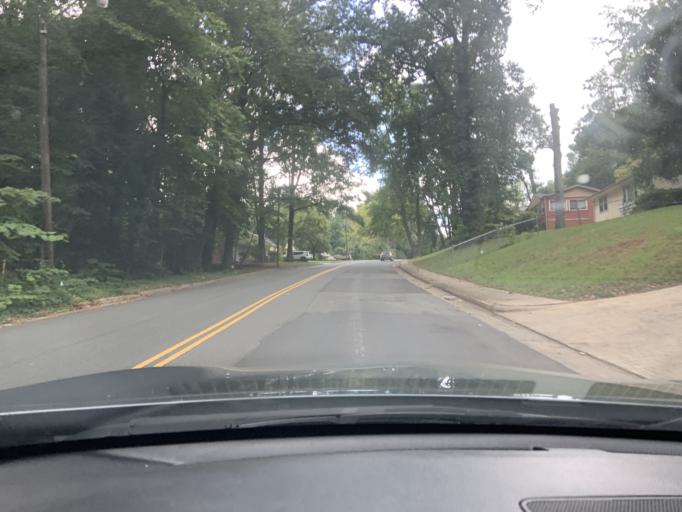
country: US
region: North Carolina
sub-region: Mecklenburg County
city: Charlotte
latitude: 35.2335
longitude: -80.8824
